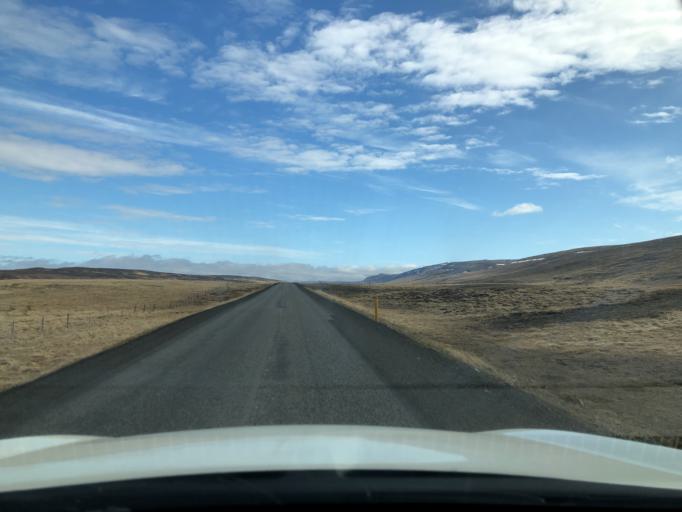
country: IS
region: West
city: Borgarnes
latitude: 65.1108
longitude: -21.6918
